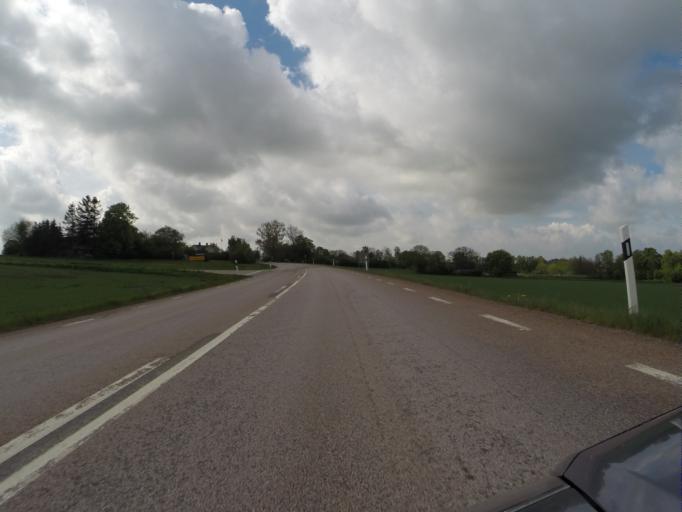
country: SE
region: Skane
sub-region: Bjuvs Kommun
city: Billesholm
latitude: 55.9825
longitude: 12.9359
